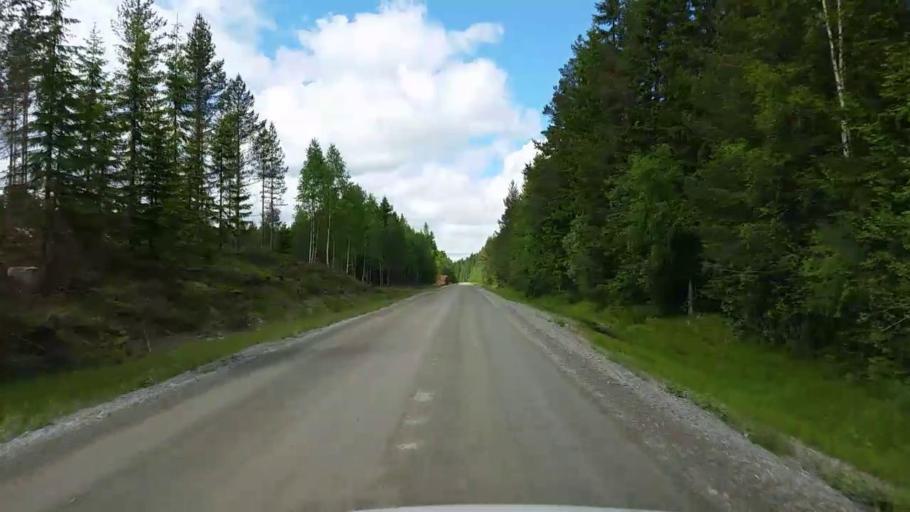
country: SE
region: Gaevleborg
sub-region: Bollnas Kommun
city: Vittsjo
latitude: 61.0390
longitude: 16.3553
